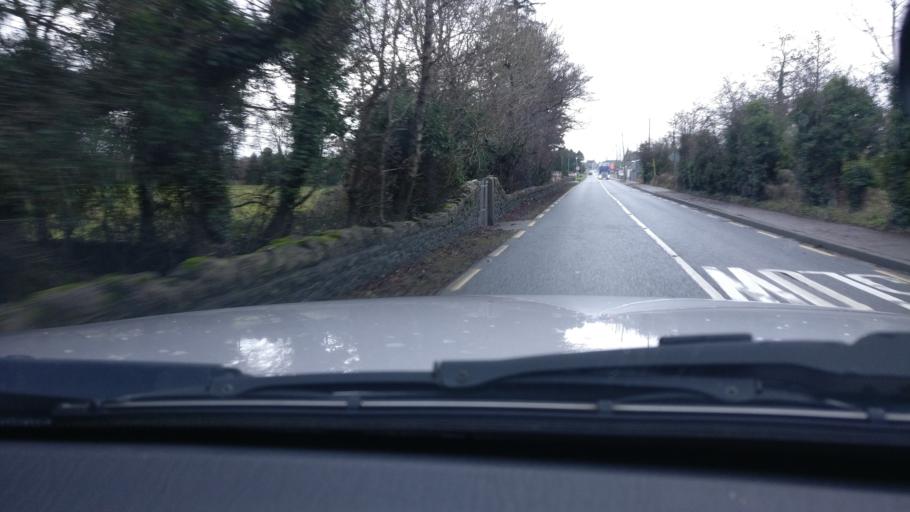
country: IE
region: Leinster
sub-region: An Longfort
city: Ballymahon
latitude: 53.5708
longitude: -7.7577
